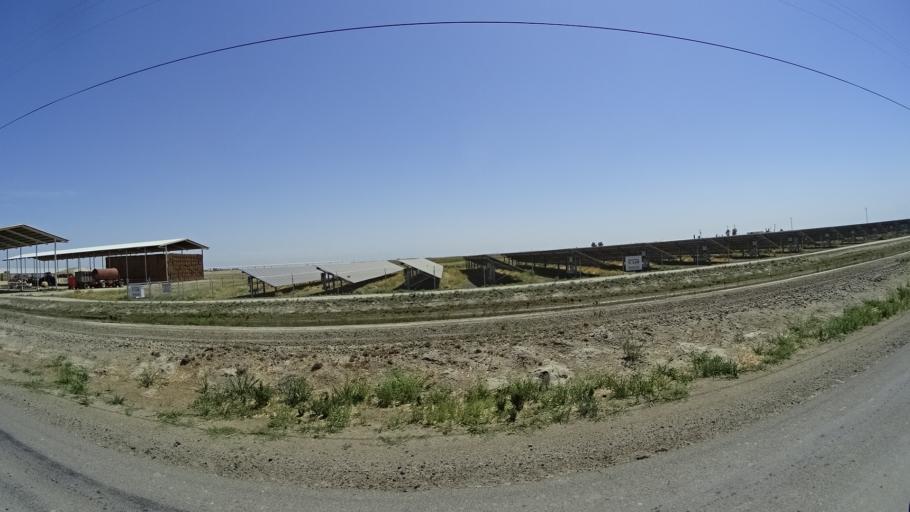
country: US
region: California
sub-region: Kings County
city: Stratford
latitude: 36.2063
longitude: -119.7624
